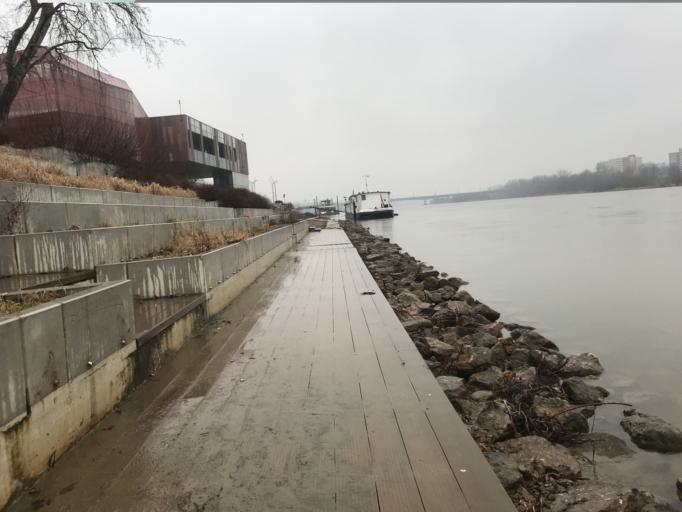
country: PL
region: Masovian Voivodeship
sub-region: Warszawa
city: Praga Polnoc
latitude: 52.2417
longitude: 21.0309
